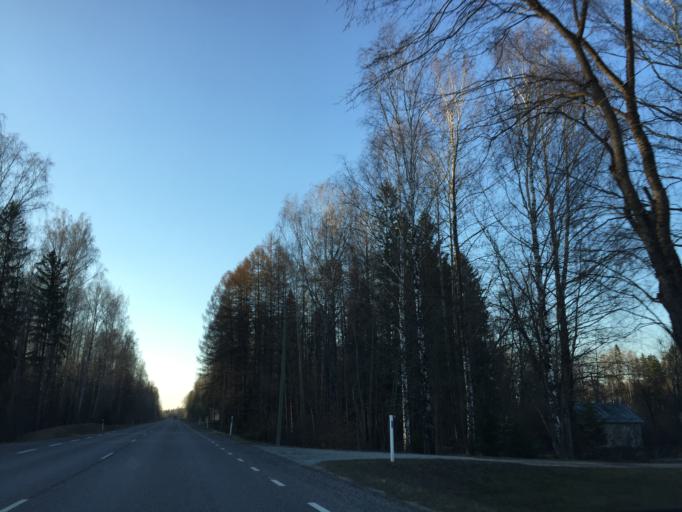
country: EE
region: Ida-Virumaa
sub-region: Johvi vald
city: Johvi
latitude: 59.3278
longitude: 27.4834
